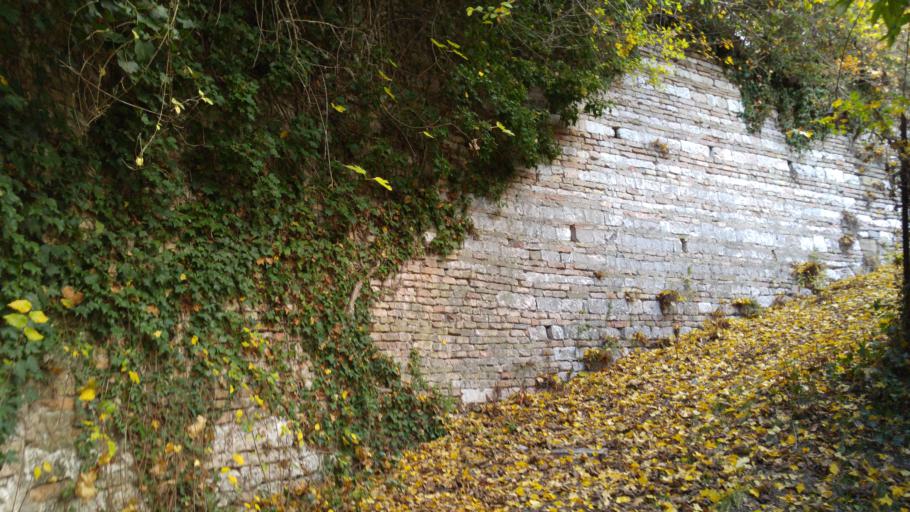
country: IT
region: The Marches
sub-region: Provincia di Pesaro e Urbino
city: Pergola
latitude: 43.5623
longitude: 12.8349
